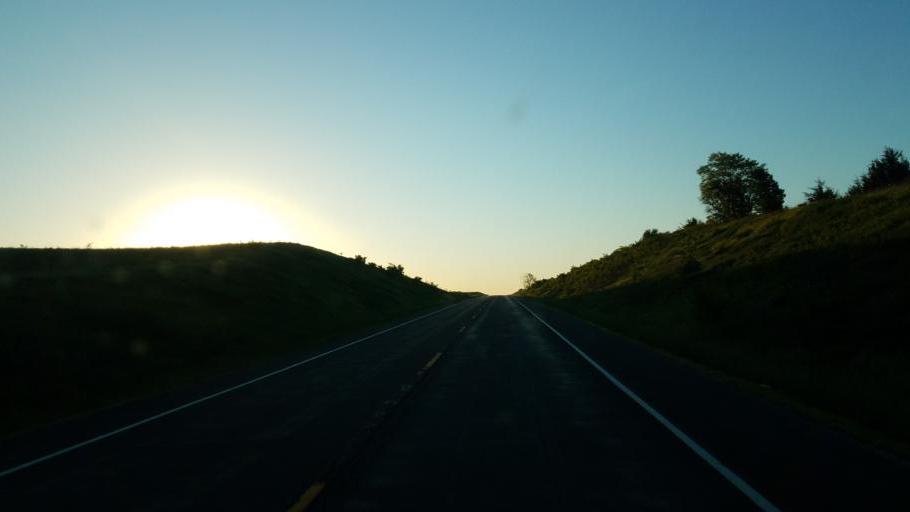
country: US
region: Missouri
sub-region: Schuyler County
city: Lancaster
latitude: 40.4926
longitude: -92.5904
